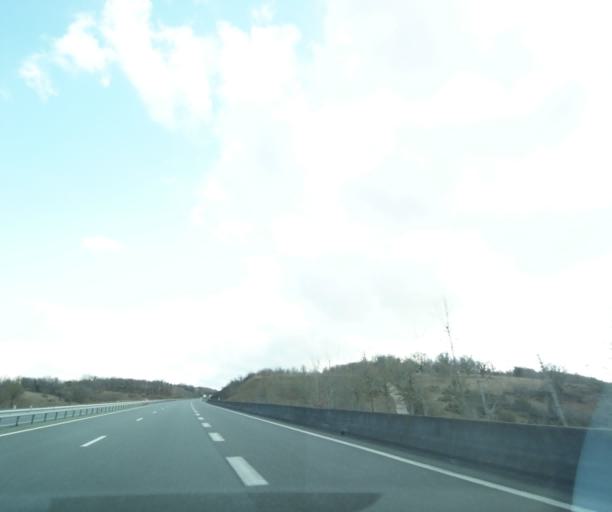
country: FR
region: Midi-Pyrenees
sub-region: Departement du Lot
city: Le Vigan
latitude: 44.7210
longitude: 1.5635
